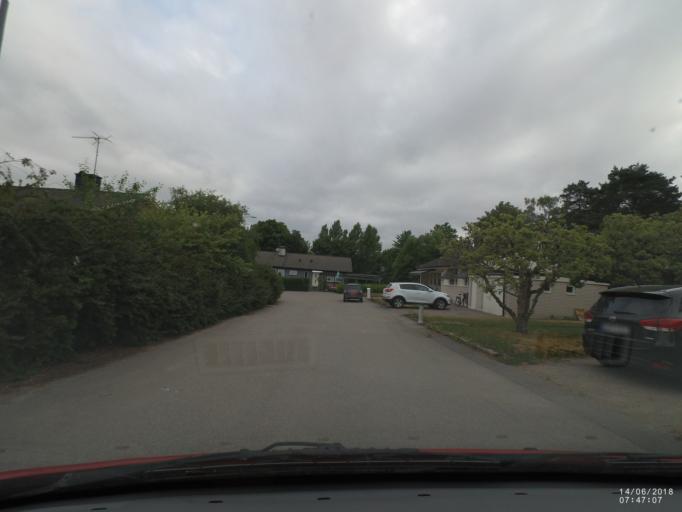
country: SE
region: Soedermanland
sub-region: Nykopings Kommun
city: Nykoping
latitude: 58.7647
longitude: 17.0133
